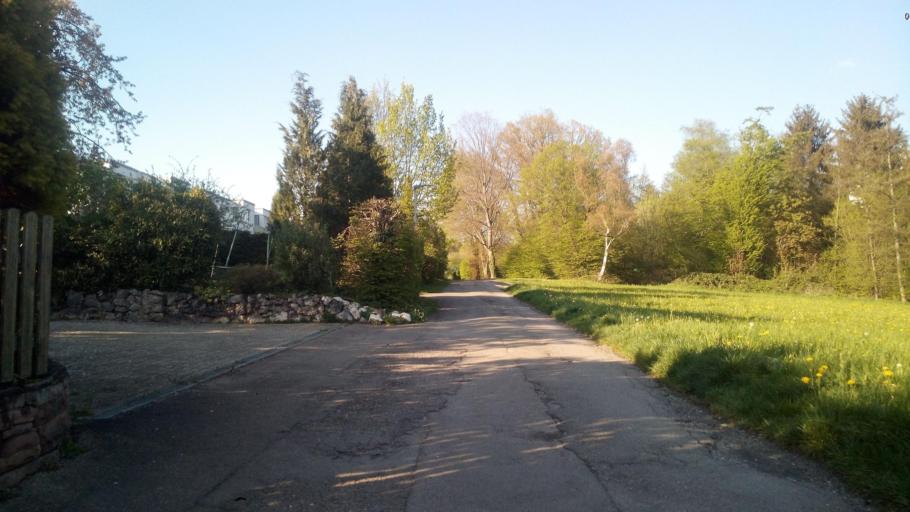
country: DE
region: Baden-Wuerttemberg
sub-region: Regierungsbezirk Stuttgart
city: Goeppingen
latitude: 48.7088
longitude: 9.6689
